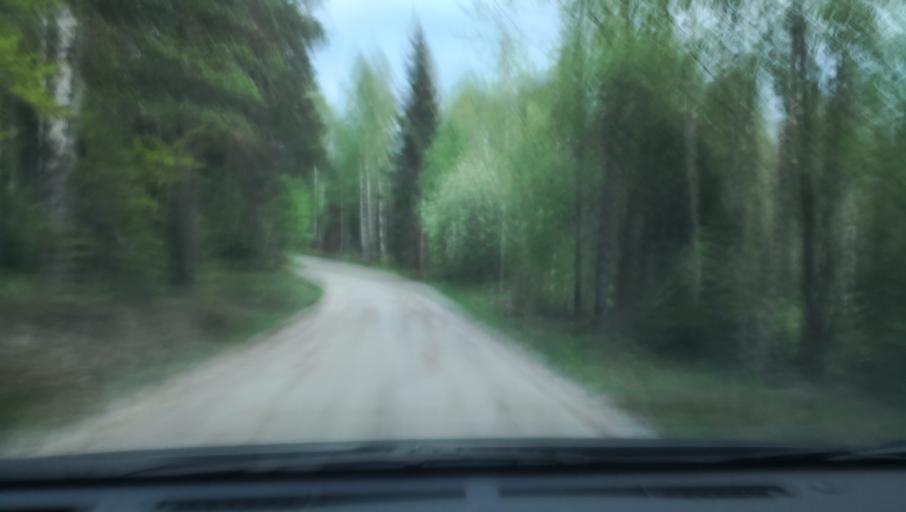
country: SE
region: Vaestmanland
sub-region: Skinnskattebergs Kommun
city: Skinnskatteberg
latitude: 59.7355
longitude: 15.4710
